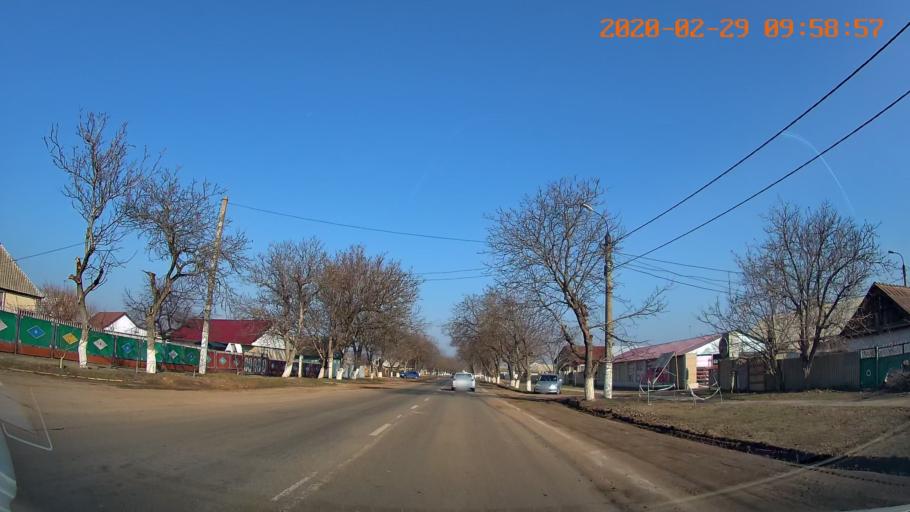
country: MD
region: Telenesti
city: Slobozia
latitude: 46.7529
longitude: 29.6894
